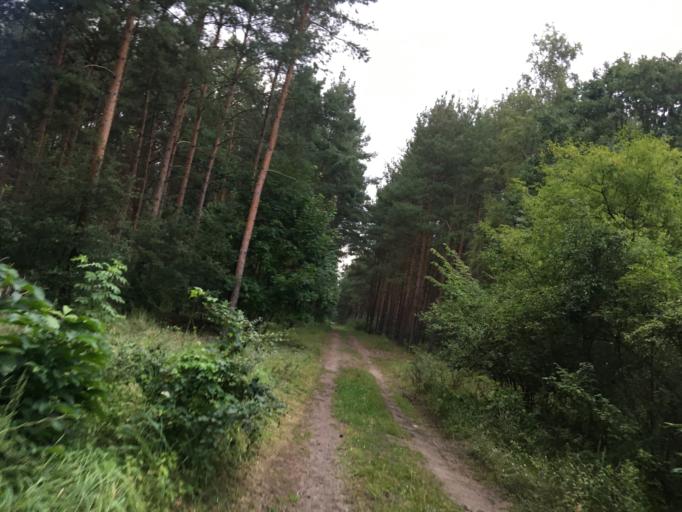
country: DE
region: Brandenburg
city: Erkner
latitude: 52.3984
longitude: 13.7663
